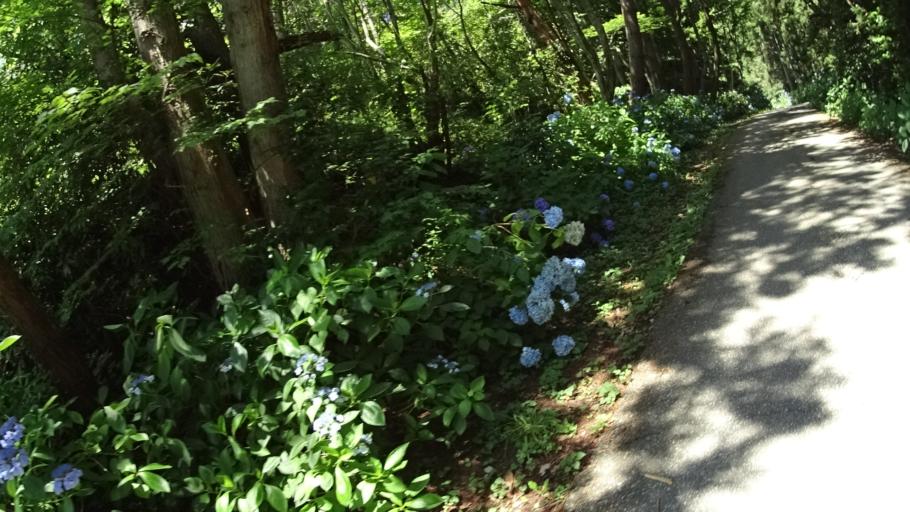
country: JP
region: Iwate
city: Ofunato
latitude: 38.8374
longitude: 141.6259
